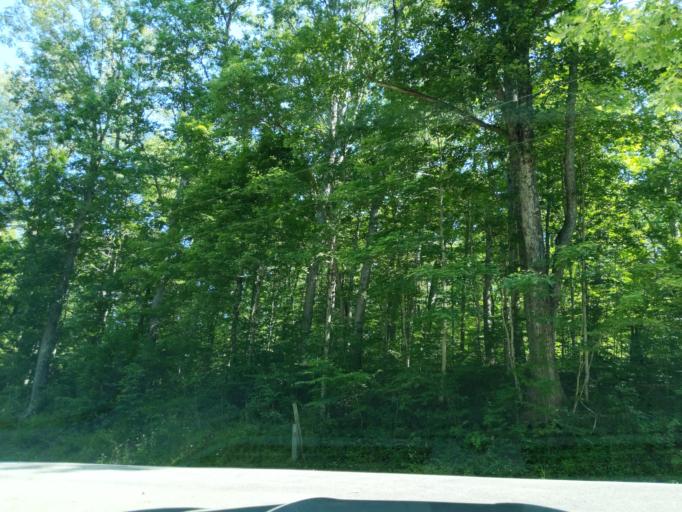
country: US
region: Indiana
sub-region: Ripley County
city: Osgood
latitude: 39.0742
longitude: -85.4241
